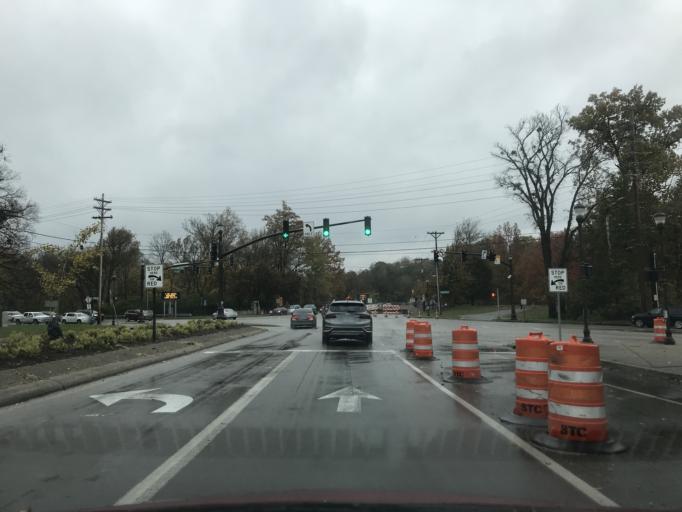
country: US
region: Kentucky
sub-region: Jefferson County
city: Saint Matthews
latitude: 38.2455
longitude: -85.7023
